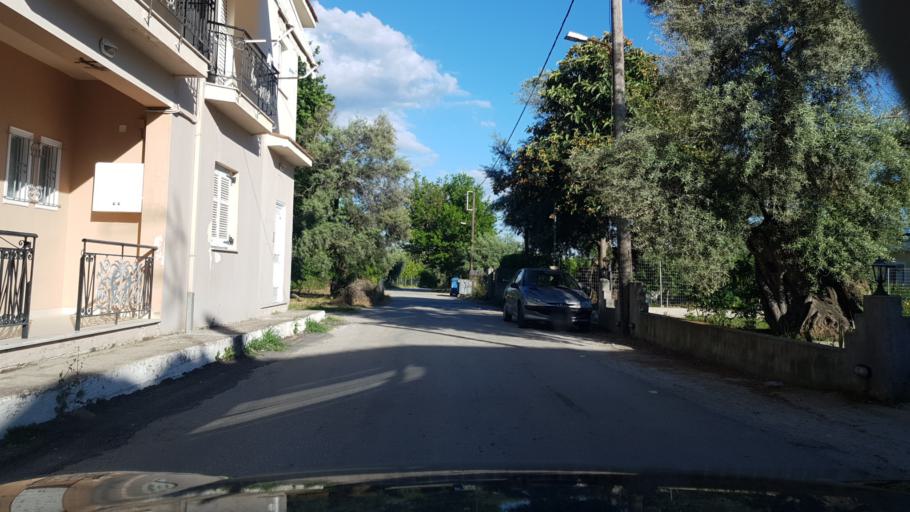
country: GR
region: Ionian Islands
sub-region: Lefkada
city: Nidri
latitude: 38.7150
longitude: 20.7007
